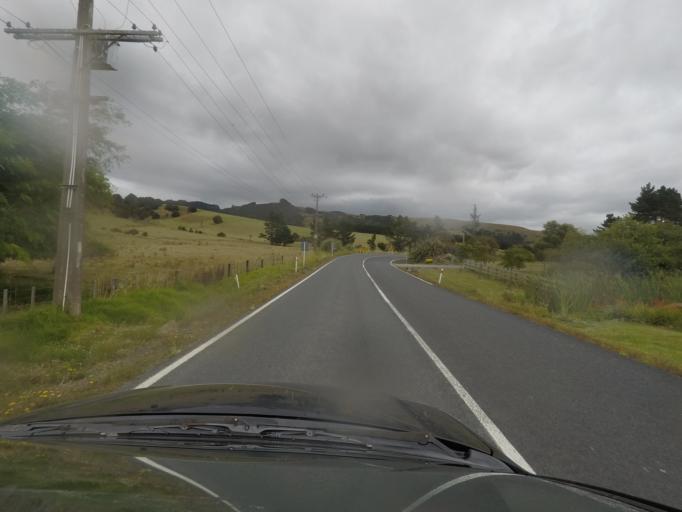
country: NZ
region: Auckland
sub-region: Auckland
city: Warkworth
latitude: -36.2886
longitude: 174.6592
